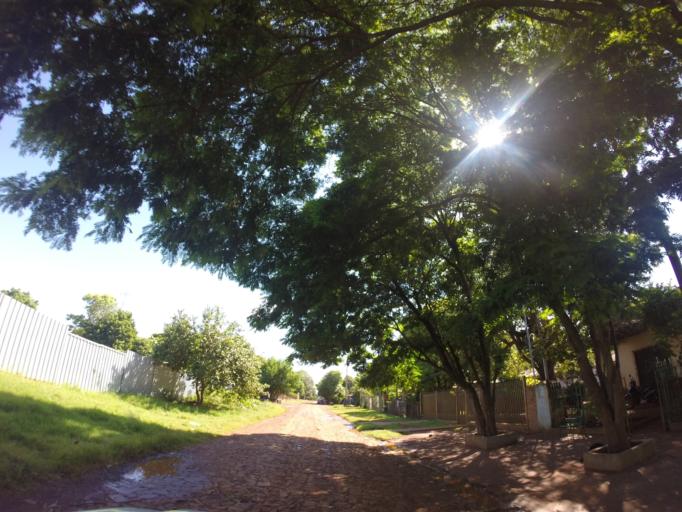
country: PY
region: Alto Parana
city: Ciudad del Este
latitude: -25.4311
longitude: -54.6423
